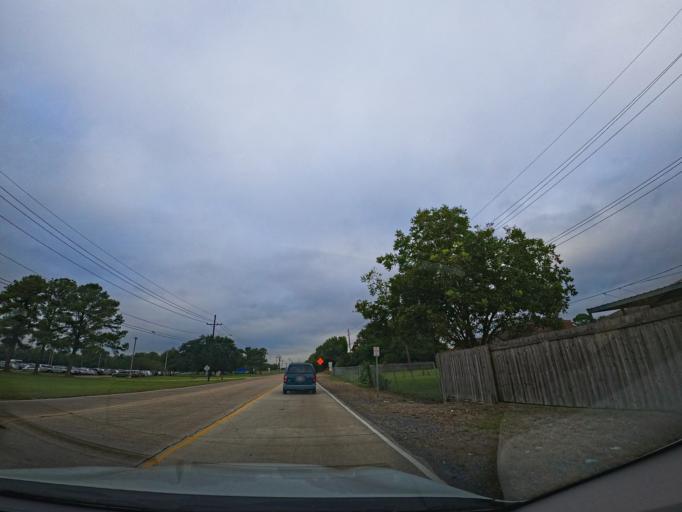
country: US
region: Louisiana
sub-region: Terrebonne Parish
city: Houma
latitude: 29.5713
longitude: -90.6874
